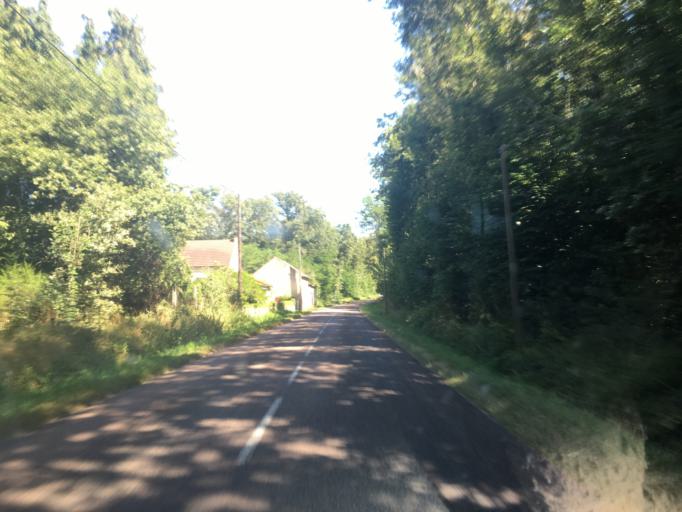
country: FR
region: Bourgogne
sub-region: Departement de l'Yonne
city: Fleury-la-Vallee
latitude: 47.8548
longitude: 3.4647
